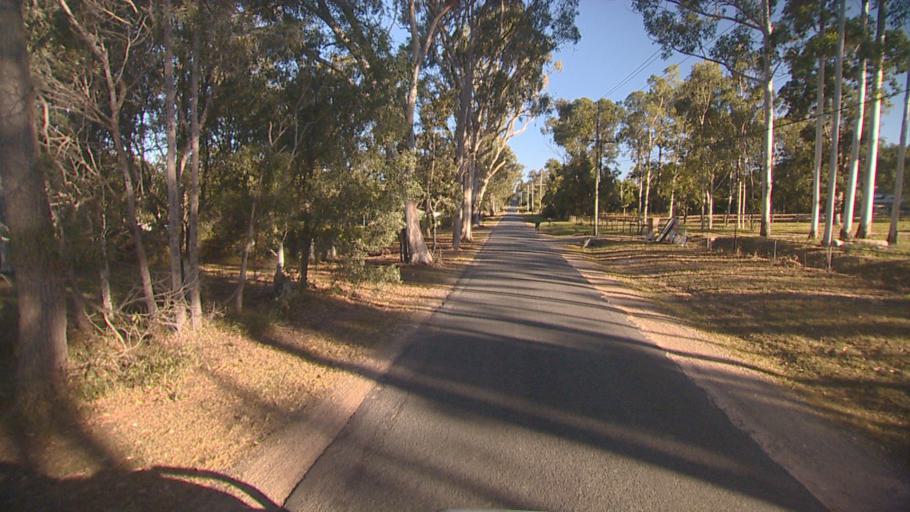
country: AU
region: Queensland
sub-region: Logan
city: Chambers Flat
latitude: -27.7798
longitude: 153.0875
